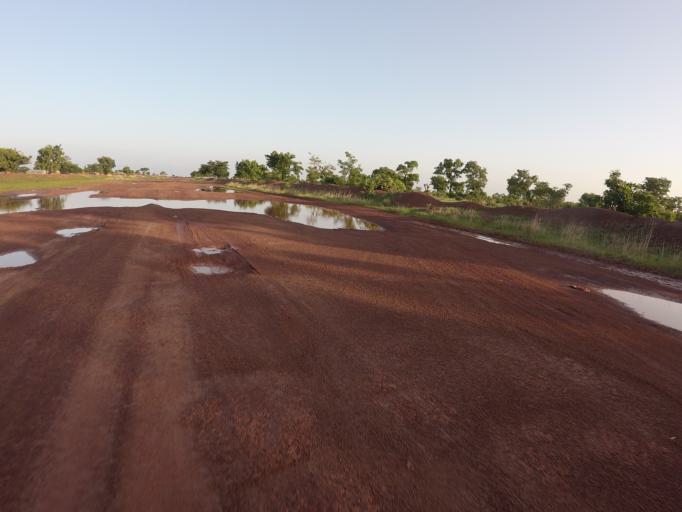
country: TG
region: Savanes
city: Sansanne-Mango
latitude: 10.2325
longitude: -0.0729
